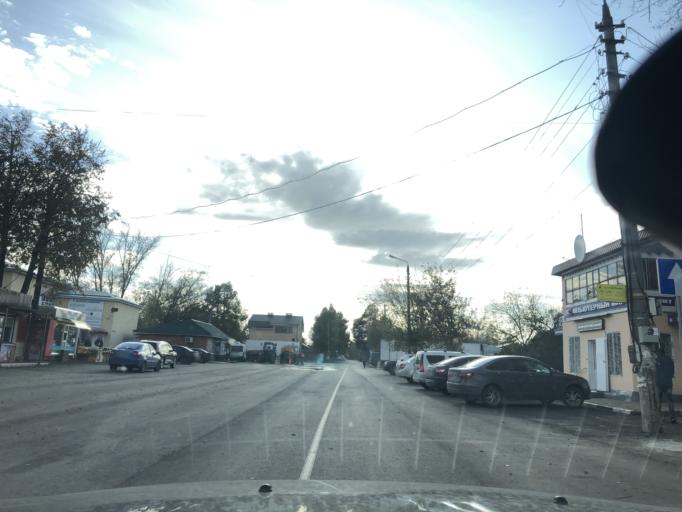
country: RU
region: Tula
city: Kireyevsk
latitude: 53.9347
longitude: 37.9285
